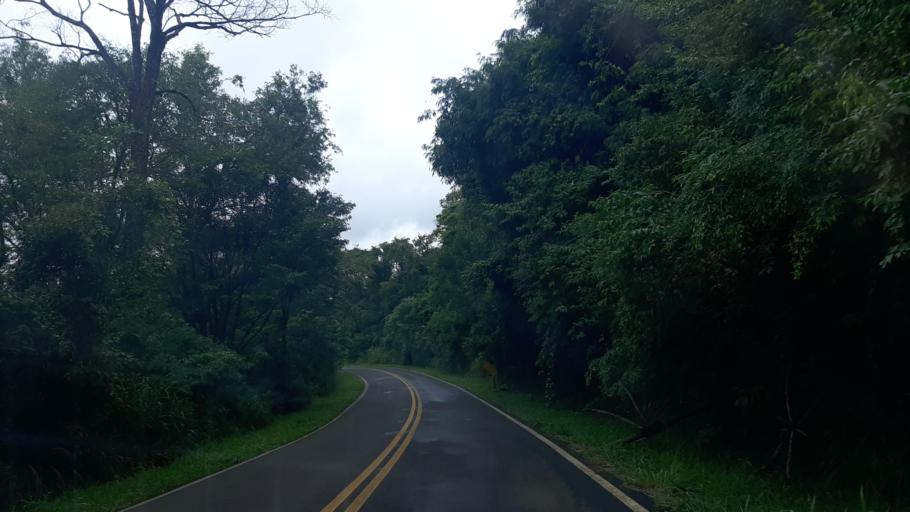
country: BR
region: Parana
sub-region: Ampere
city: Ampere
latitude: -25.9680
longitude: -53.4439
